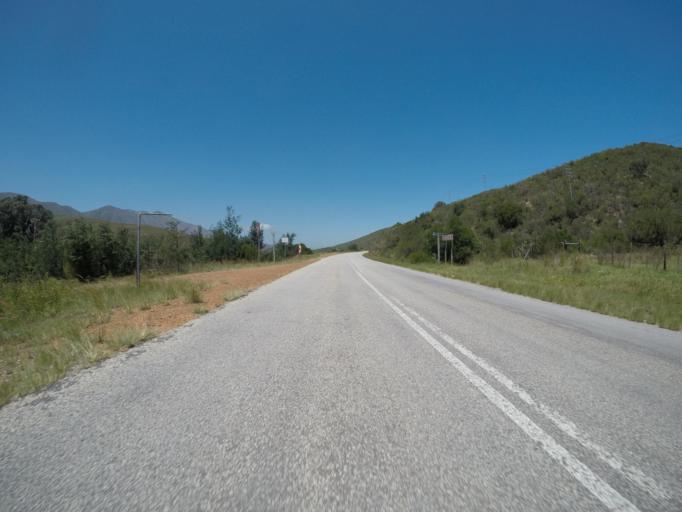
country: ZA
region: Eastern Cape
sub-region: Cacadu District Municipality
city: Kareedouw
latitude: -33.9029
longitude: 24.1337
